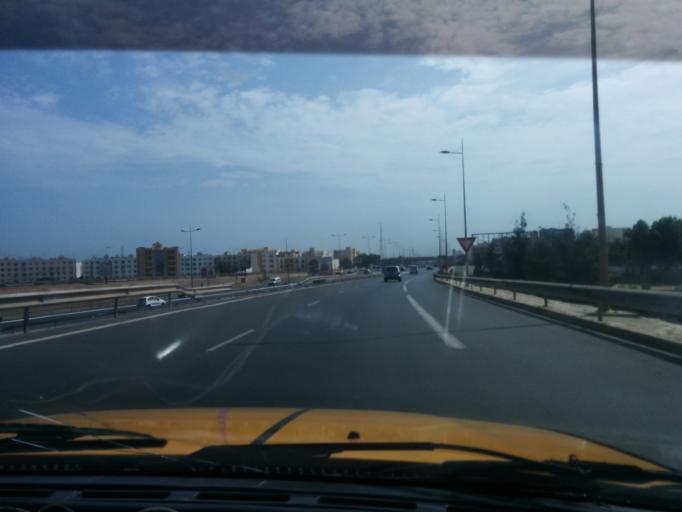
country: SN
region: Dakar
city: Grand Dakar
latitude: 14.7398
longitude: -17.4396
